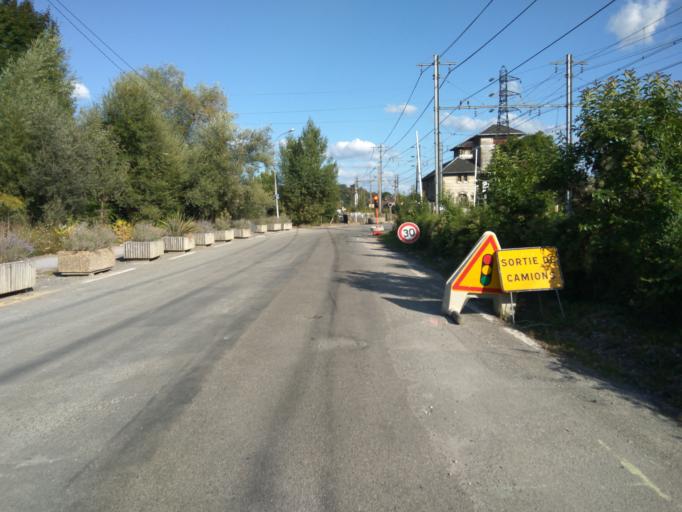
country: FR
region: Aquitaine
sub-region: Departement des Pyrenees-Atlantiques
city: Gelos
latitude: 43.2898
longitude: -0.3612
